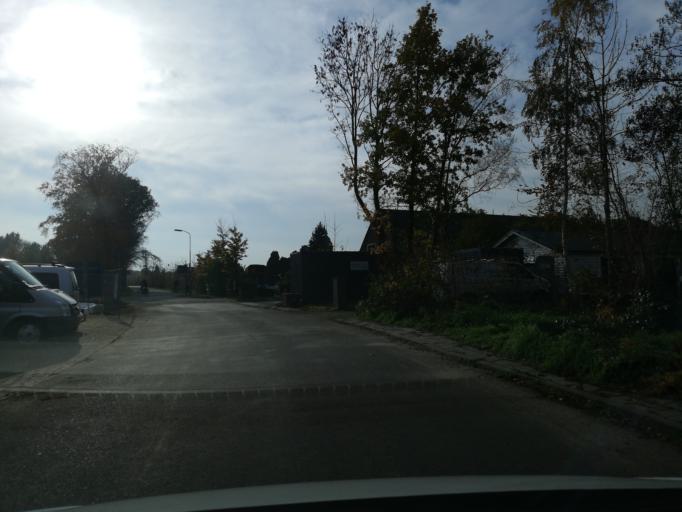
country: NL
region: Gelderland
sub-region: Gemeente Voorst
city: Twello
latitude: 52.2397
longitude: 6.0461
